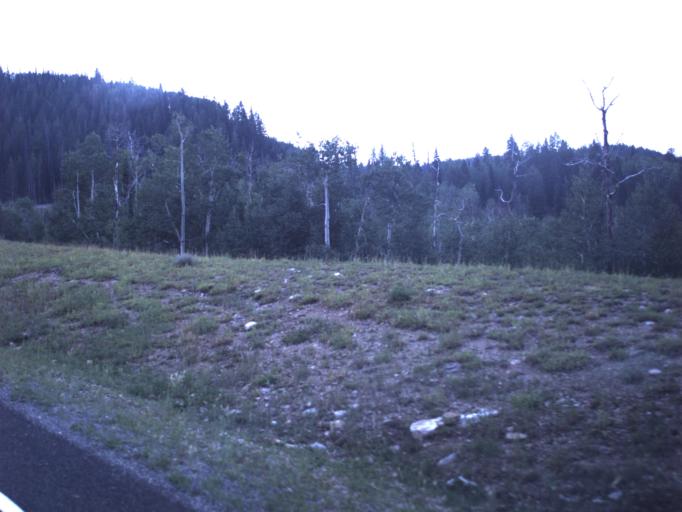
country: US
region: Utah
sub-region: Summit County
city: Francis
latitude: 40.5130
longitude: -111.0456
